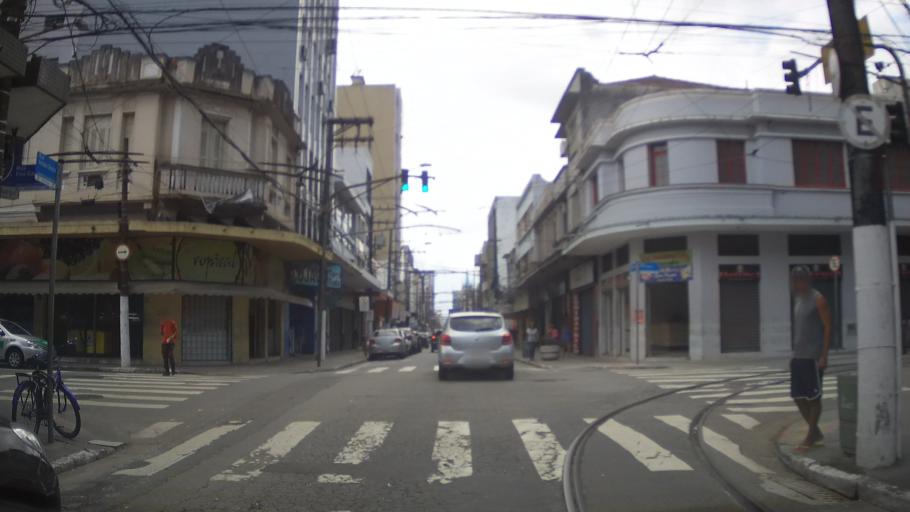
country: BR
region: Sao Paulo
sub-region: Santos
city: Santos
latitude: -23.9354
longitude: -46.3307
